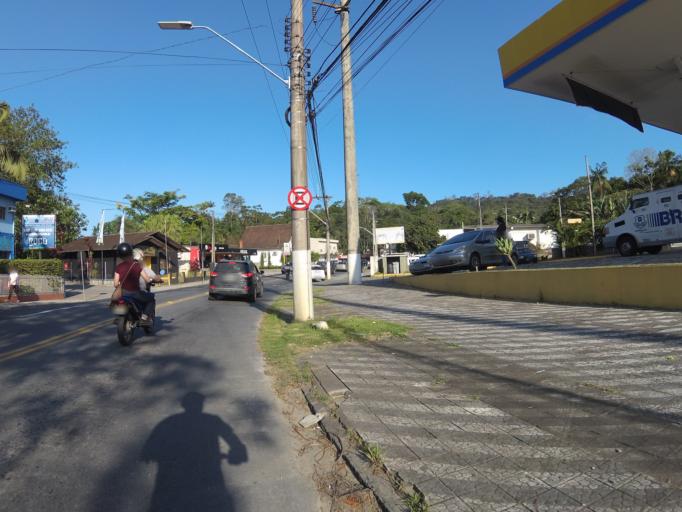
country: BR
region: Santa Catarina
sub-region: Blumenau
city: Blumenau
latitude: -26.9196
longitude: -49.0965
